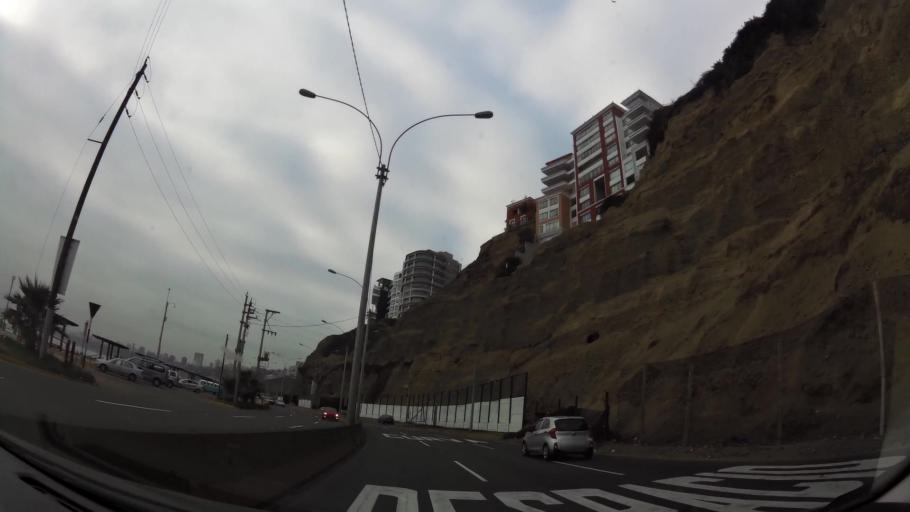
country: PE
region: Lima
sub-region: Lima
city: Surco
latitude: -12.1532
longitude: -77.0245
